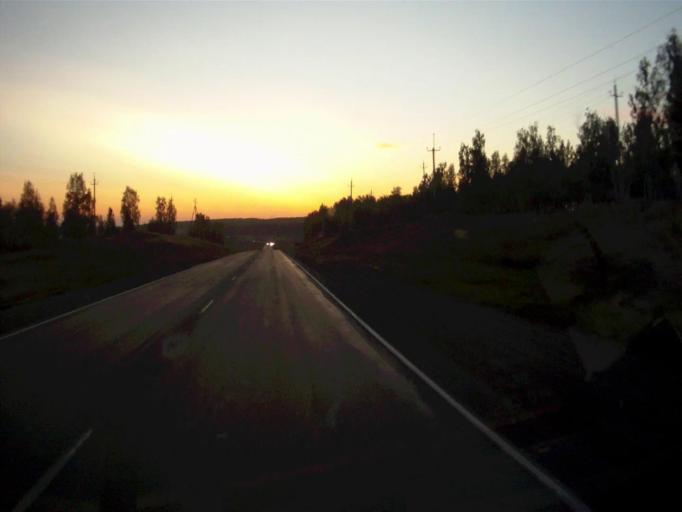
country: RU
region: Chelyabinsk
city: Poletayevo
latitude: 55.2226
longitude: 61.0121
